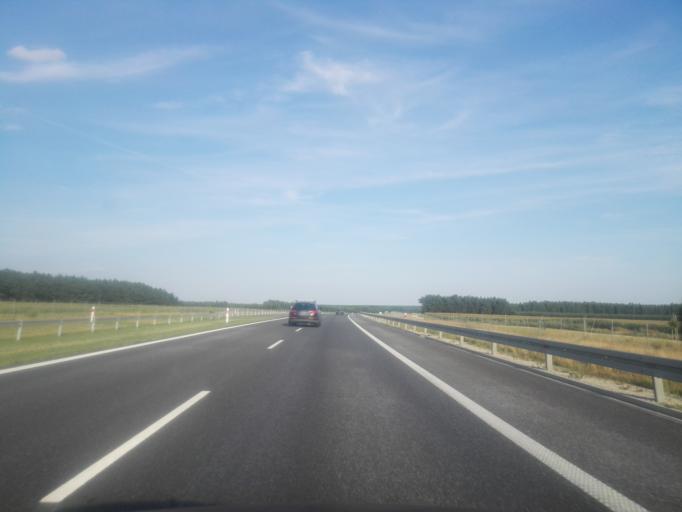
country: PL
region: Lodz Voivodeship
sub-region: Powiat wieruszowski
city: Wieruszow
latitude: 51.3361
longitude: 18.1332
